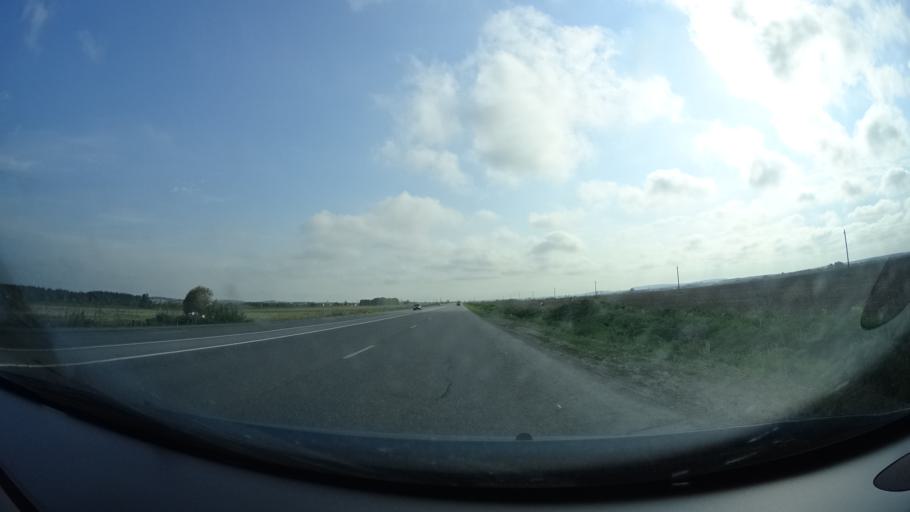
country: RU
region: Perm
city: Kultayevo
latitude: 57.8774
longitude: 55.9078
